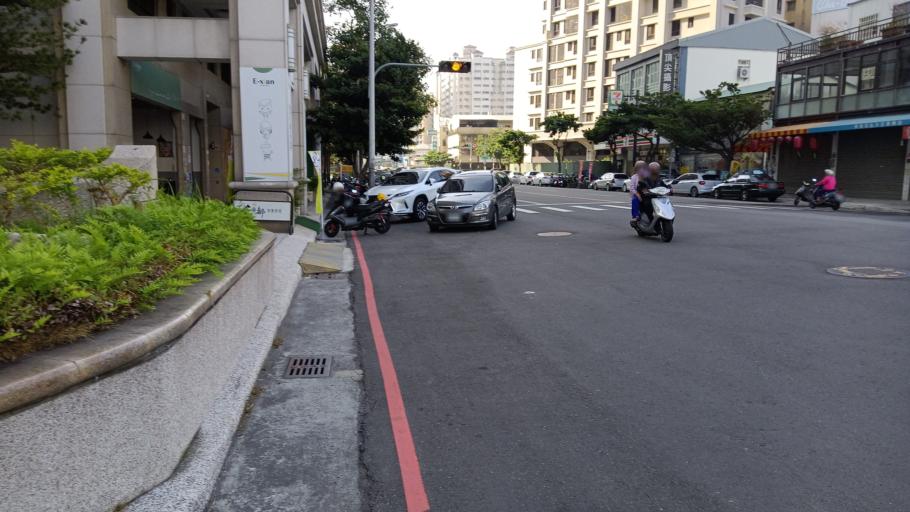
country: TW
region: Taiwan
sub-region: Taichung City
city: Taichung
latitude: 24.1189
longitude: 120.6570
